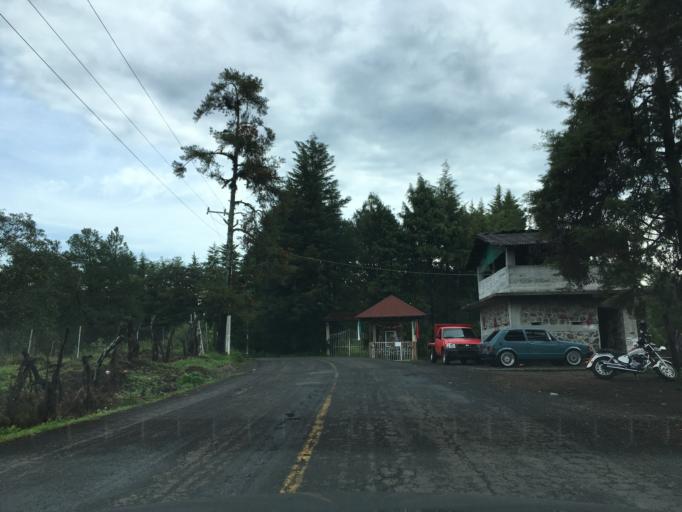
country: MX
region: Michoacan
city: Nuevo San Juan Parangaricutiro
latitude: 19.4308
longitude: -102.1420
